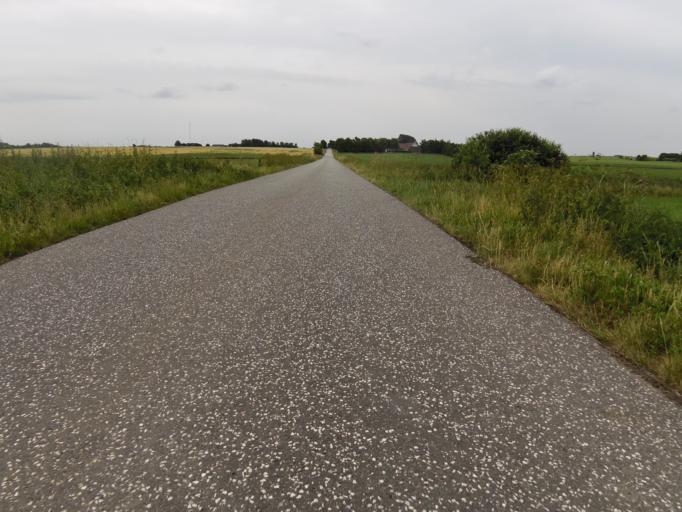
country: DK
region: Central Jutland
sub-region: Holstebro Kommune
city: Holstebro
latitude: 56.4154
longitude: 8.6720
